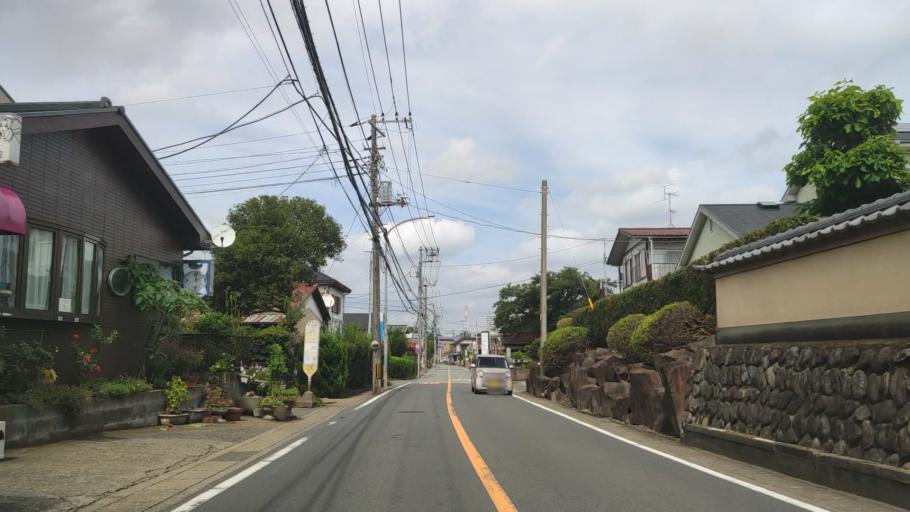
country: JP
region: Kanagawa
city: Minami-rinkan
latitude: 35.4878
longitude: 139.4729
